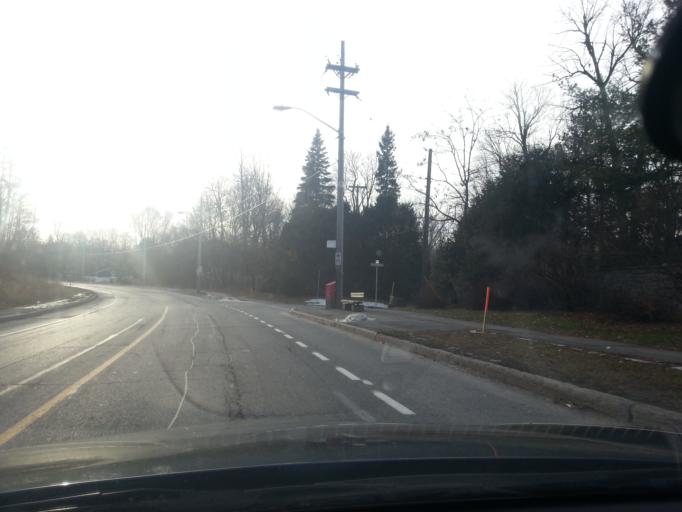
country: CA
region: Quebec
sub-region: Outaouais
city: Gatineau
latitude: 45.4478
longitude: -75.6680
